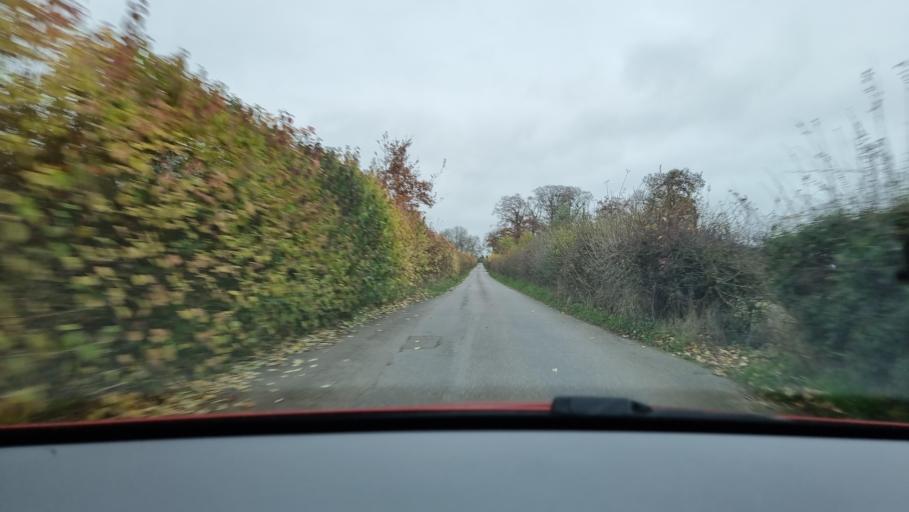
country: GB
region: England
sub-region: Oxfordshire
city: Woodstock
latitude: 51.8744
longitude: -1.3126
